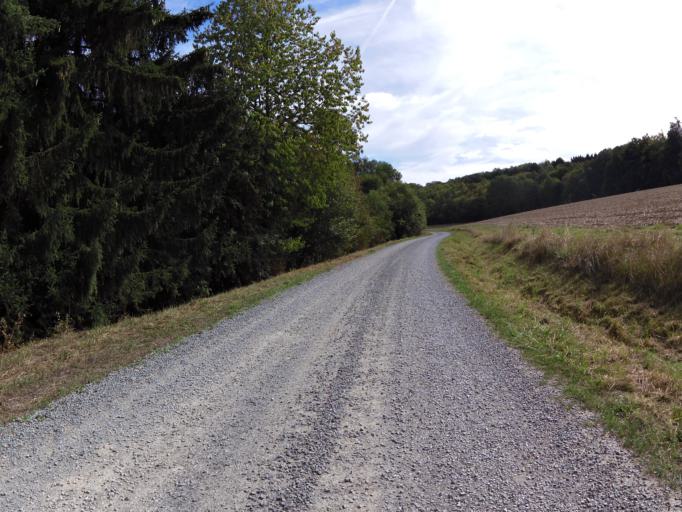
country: DE
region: Bavaria
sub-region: Regierungsbezirk Unterfranken
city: Hettstadt
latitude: 49.7801
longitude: 9.8164
